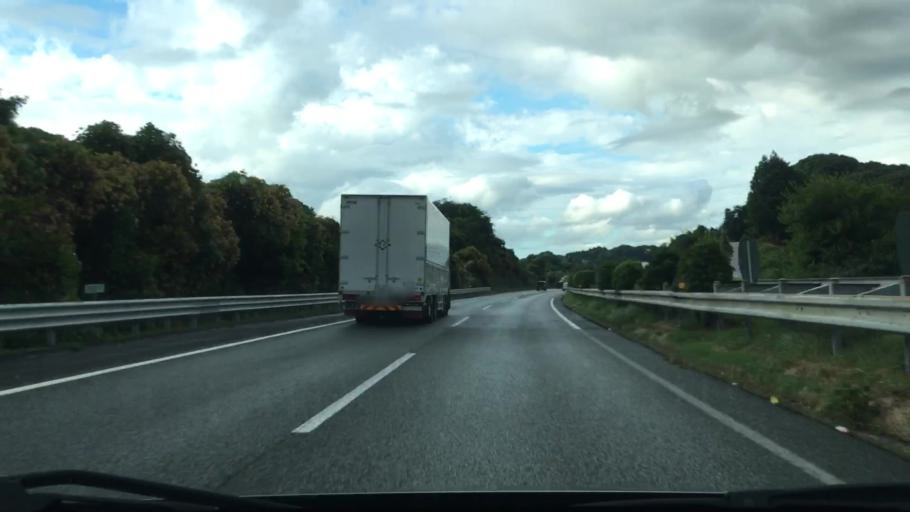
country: JP
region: Fukuoka
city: Koga
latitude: 33.7032
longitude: 130.4851
